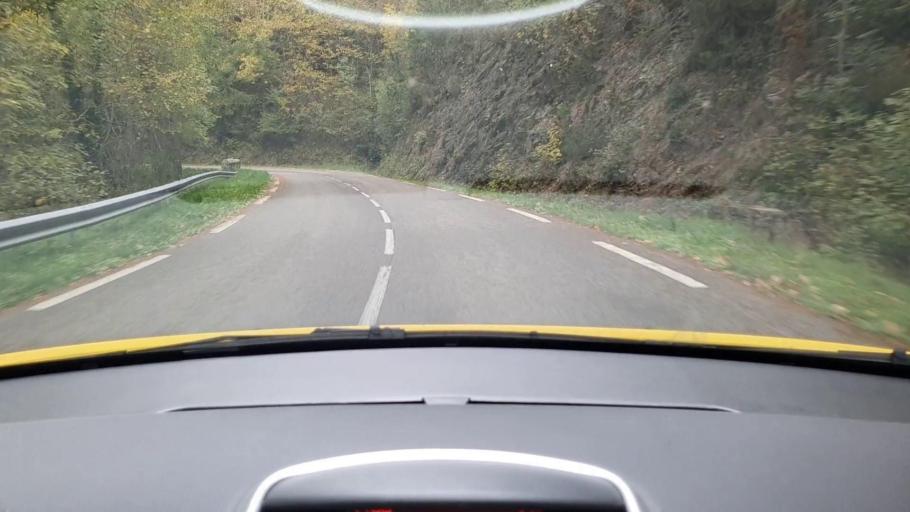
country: FR
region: Languedoc-Roussillon
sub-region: Departement de la Lozere
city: Meyrueis
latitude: 44.1334
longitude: 3.4287
